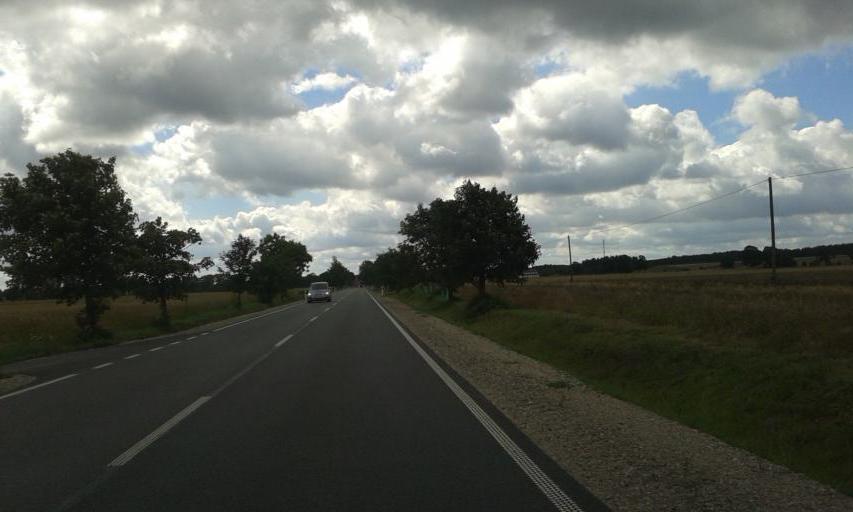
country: PL
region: West Pomeranian Voivodeship
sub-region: Powiat szczecinecki
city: Lubowo
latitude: 53.4932
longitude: 16.3361
